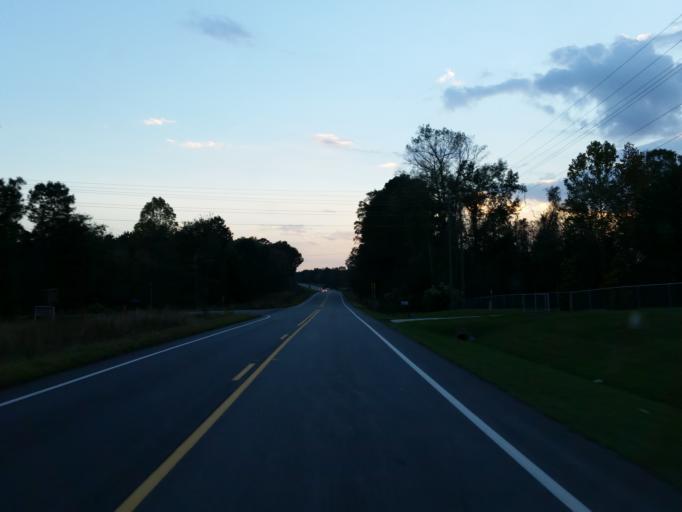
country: US
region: Georgia
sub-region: Pulaski County
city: Hawkinsville
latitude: 32.2570
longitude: -83.4913
